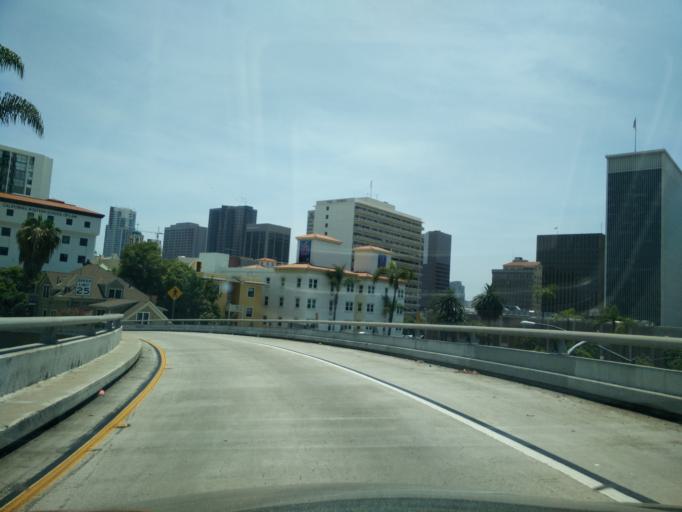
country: US
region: California
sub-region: San Diego County
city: San Diego
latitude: 32.7221
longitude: -117.1641
